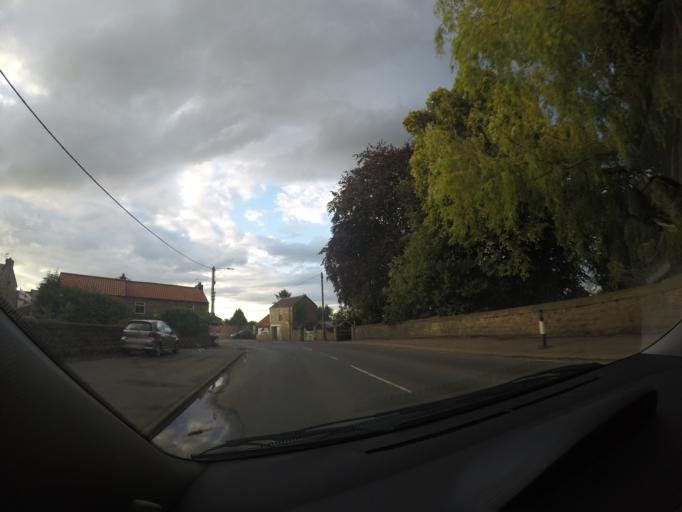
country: GB
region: England
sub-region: North Yorkshire
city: Catterick
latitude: 54.3760
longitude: -1.6296
